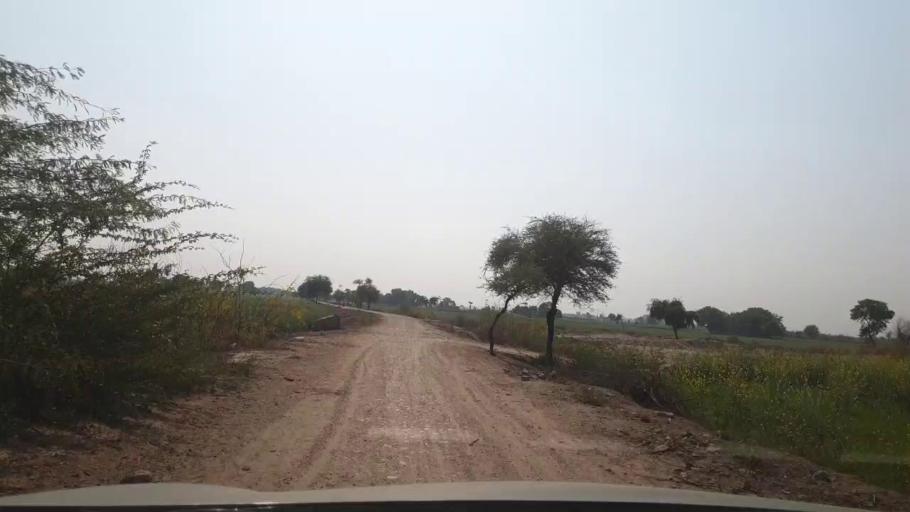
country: PK
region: Sindh
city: Tando Allahyar
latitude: 25.5385
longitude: 68.8343
